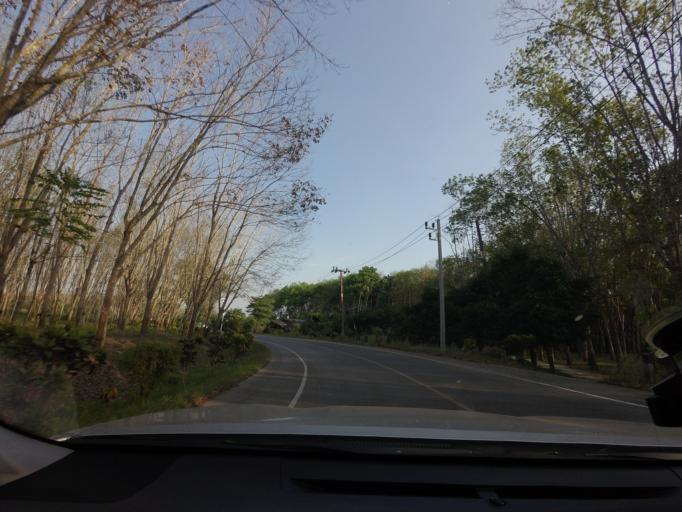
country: TH
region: Surat Thani
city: Phrasaeng
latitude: 8.5661
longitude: 99.2852
